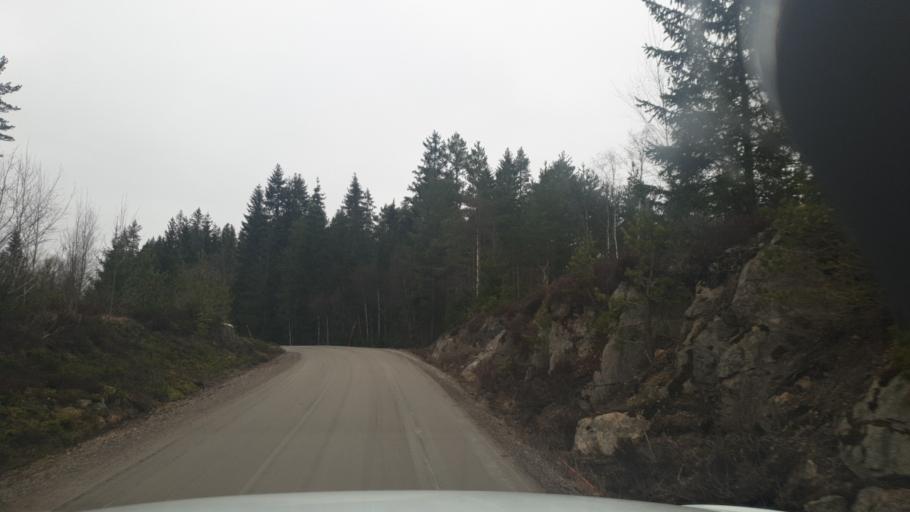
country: NO
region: Ostfold
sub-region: Romskog
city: Romskog
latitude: 59.7072
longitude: 12.0452
